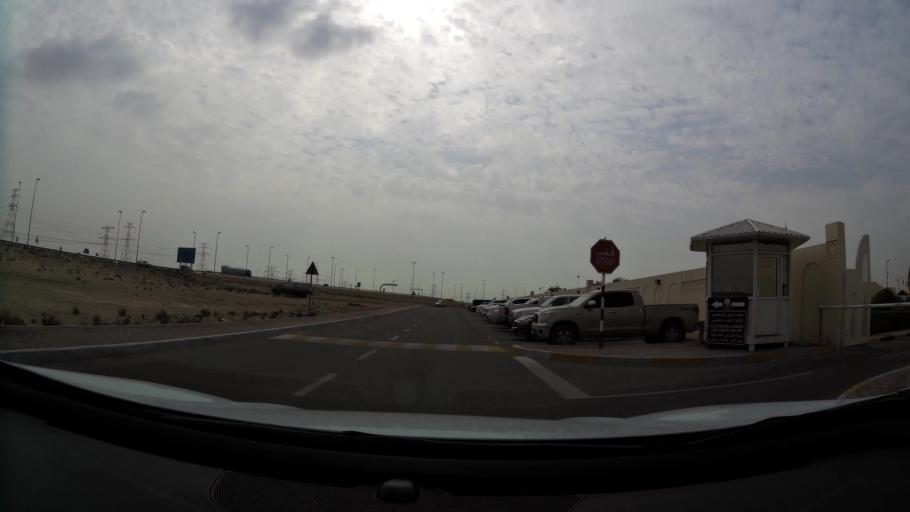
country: AE
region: Abu Dhabi
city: Abu Dhabi
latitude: 24.6590
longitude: 54.7441
